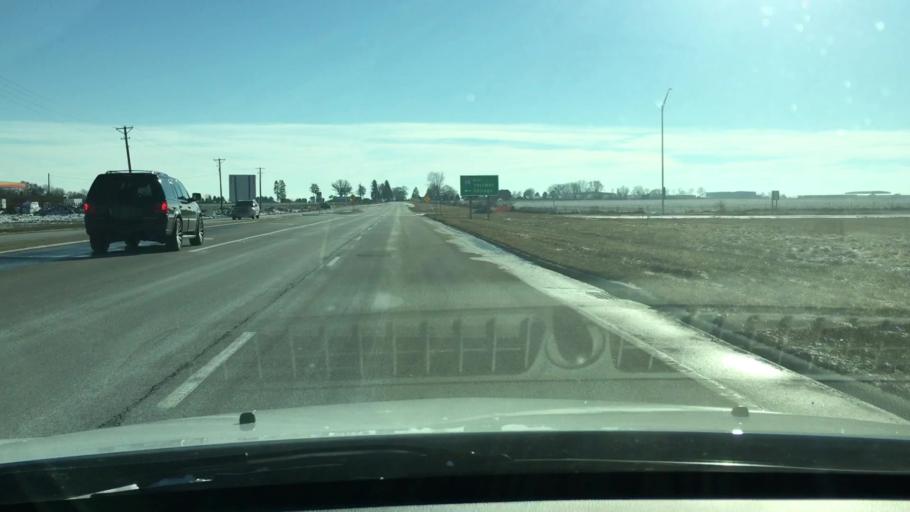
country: US
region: Illinois
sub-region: Ogle County
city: Rochelle
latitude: 41.8997
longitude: -89.0683
